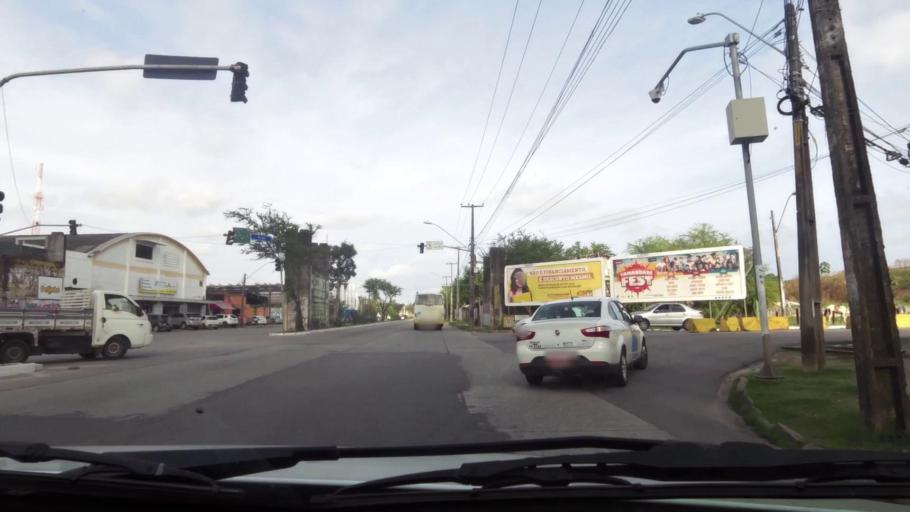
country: BR
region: Pernambuco
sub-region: Recife
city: Recife
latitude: -8.0769
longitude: -34.8947
